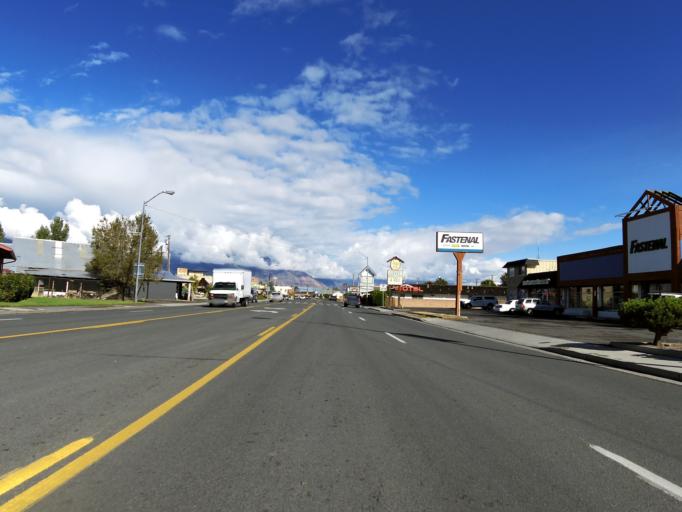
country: US
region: Nevada
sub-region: Douglas County
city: Minden
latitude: 38.9516
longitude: -119.7611
